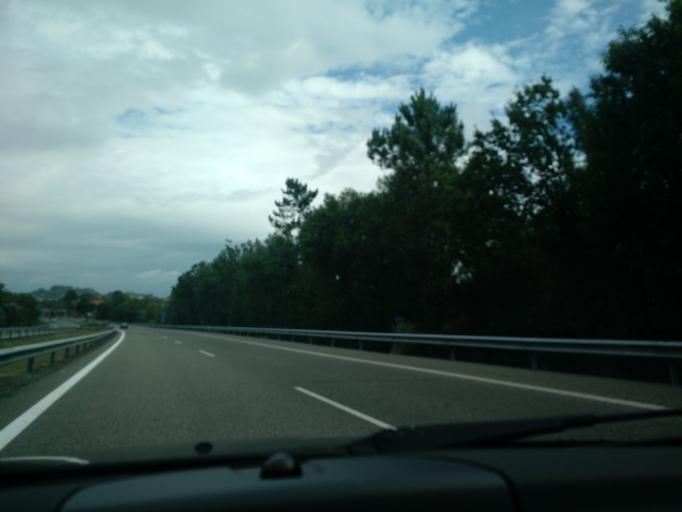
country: ES
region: Galicia
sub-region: Provincia da Coruna
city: Abegondo
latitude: 43.2517
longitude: -8.2546
